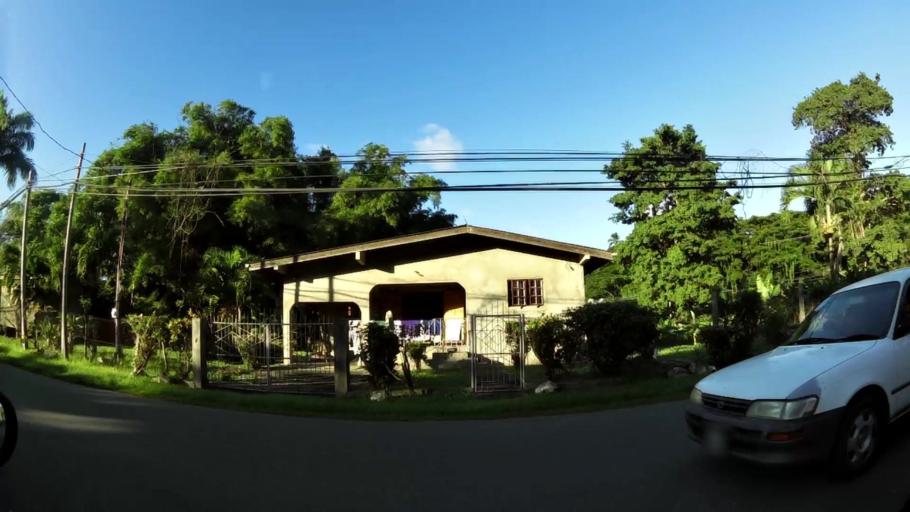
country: TT
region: Tobago
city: Scarborough
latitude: 11.2157
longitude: -60.7719
